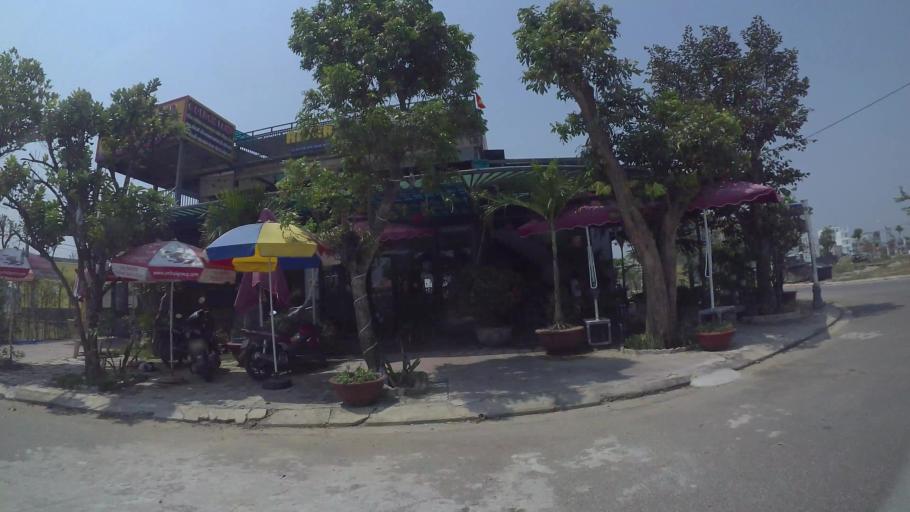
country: VN
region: Da Nang
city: Ngu Hanh Son
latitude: 15.9851
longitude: 108.2633
